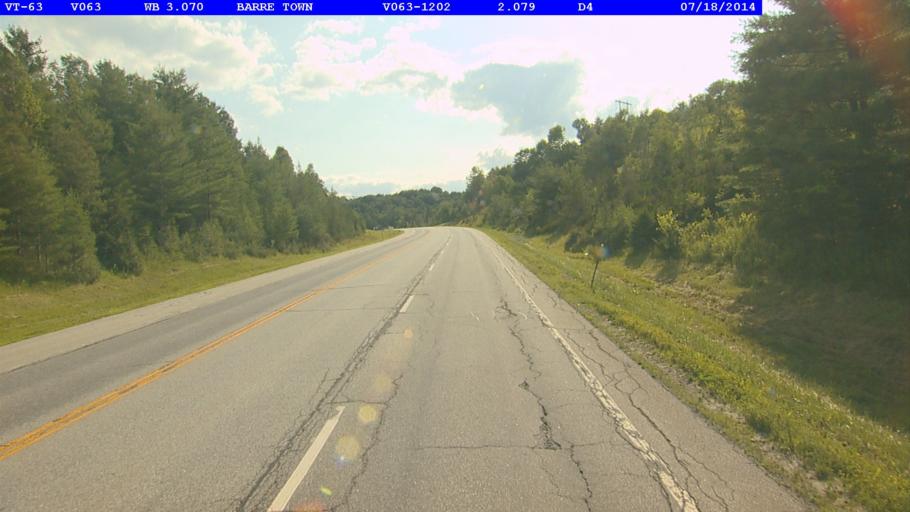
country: US
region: Vermont
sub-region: Washington County
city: South Barre
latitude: 44.1702
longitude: -72.5228
